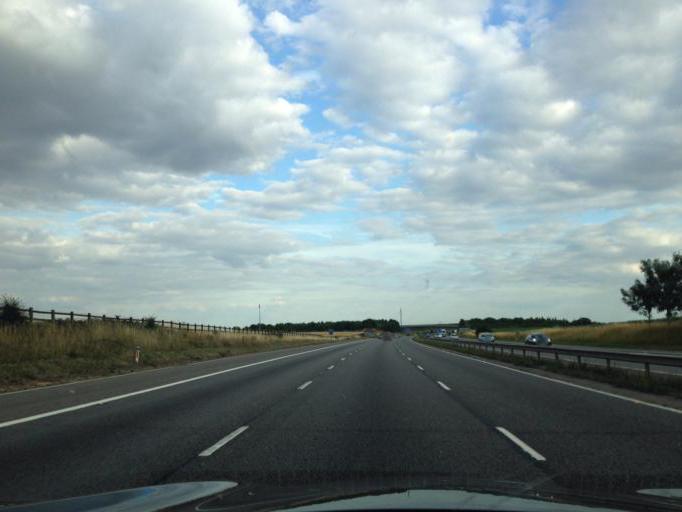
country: GB
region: England
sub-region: Oxfordshire
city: Somerton
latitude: 51.9611
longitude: -1.2204
